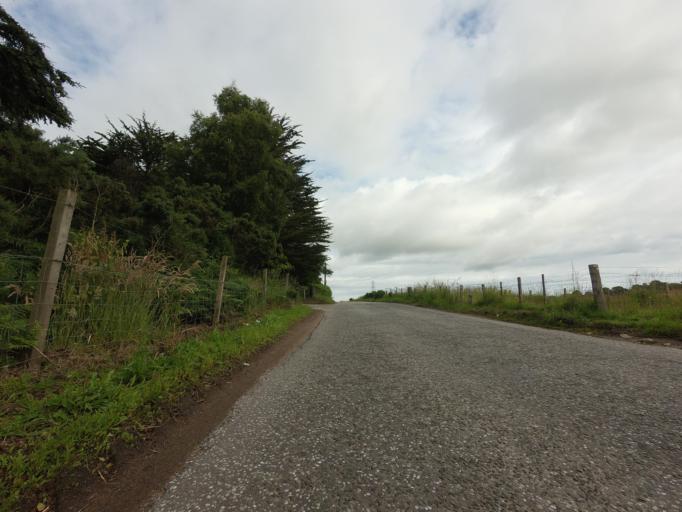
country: GB
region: Scotland
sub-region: Moray
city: Elgin
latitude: 57.6594
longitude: -3.3545
